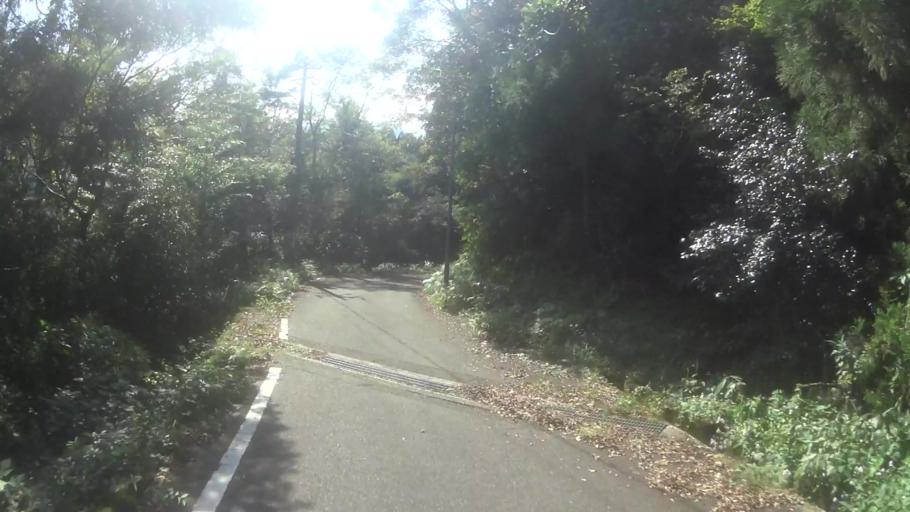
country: JP
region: Kyoto
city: Miyazu
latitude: 35.6975
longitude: 135.1576
